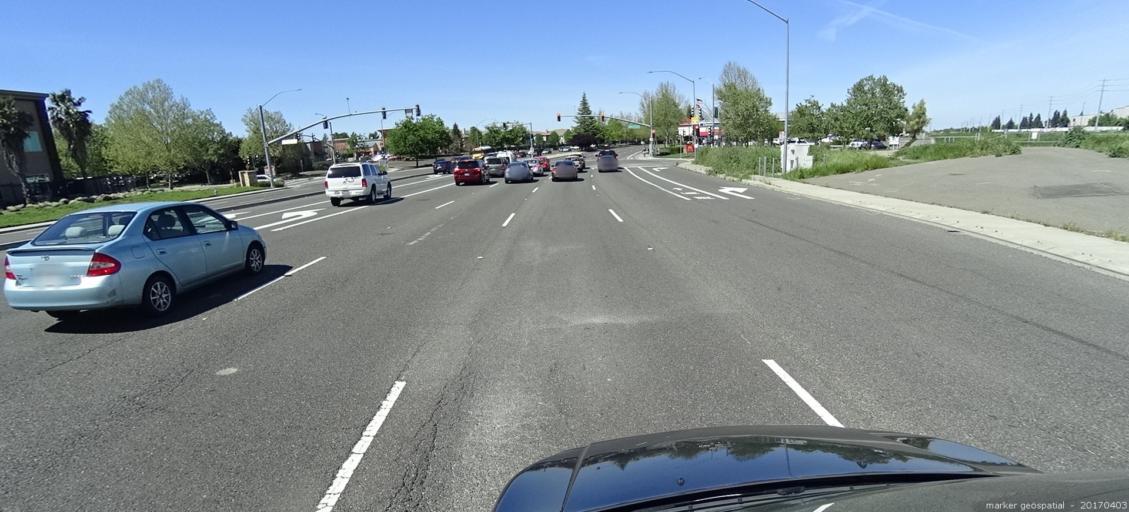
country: US
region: California
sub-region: Sacramento County
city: Sacramento
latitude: 38.6399
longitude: -121.5075
